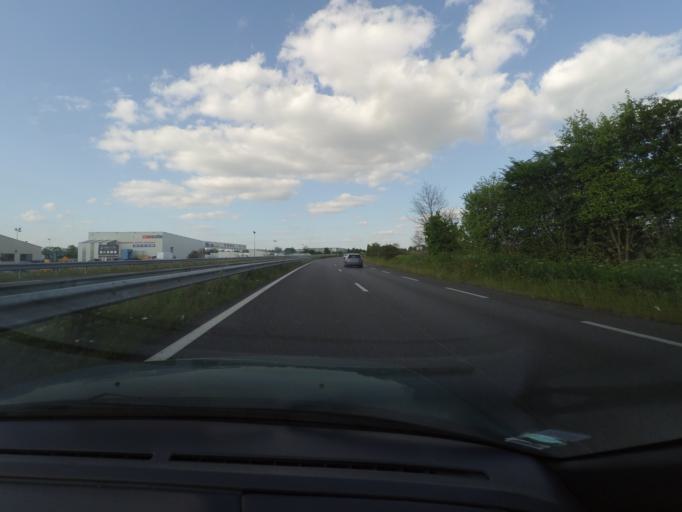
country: FR
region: Pays de la Loire
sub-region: Departement de la Vendee
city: Belleville-sur-Vie
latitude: 46.7718
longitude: -1.4289
